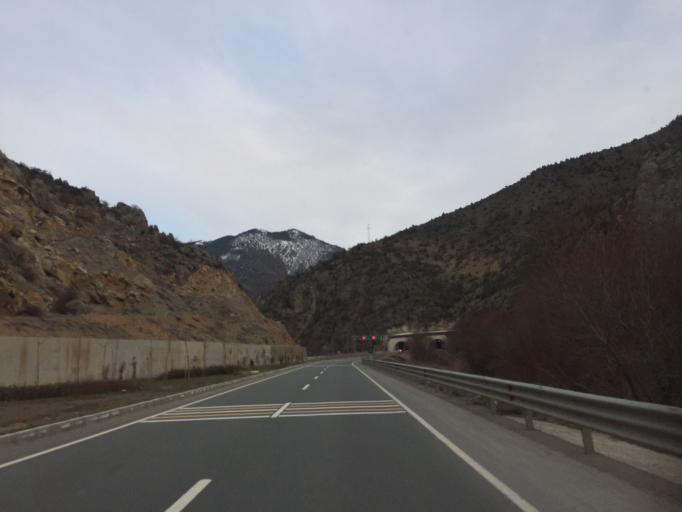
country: TR
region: Gumushane
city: Gumushkhane
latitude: 40.5196
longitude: 39.4079
